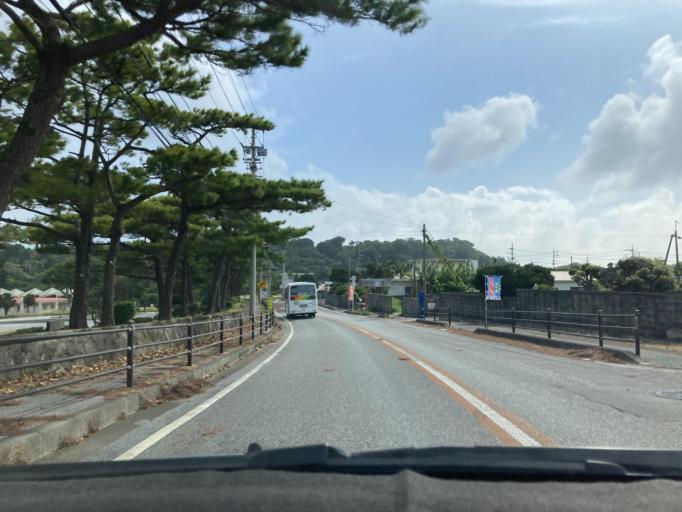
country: JP
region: Okinawa
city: Itoman
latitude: 26.0963
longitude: 127.7215
